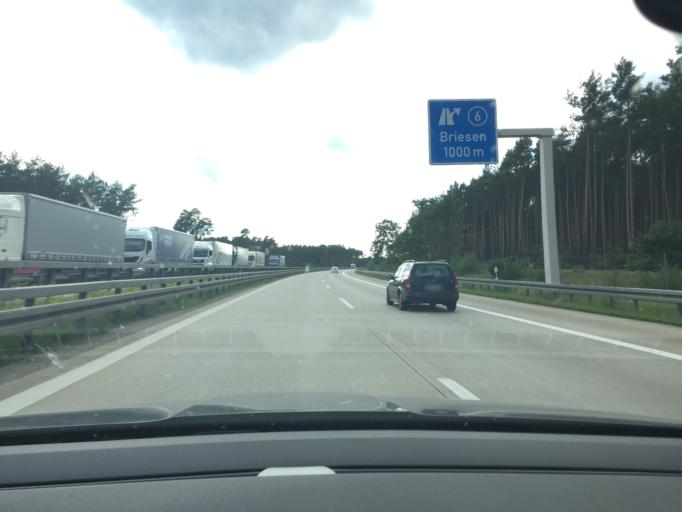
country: DE
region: Brandenburg
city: Briesen
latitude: 52.3243
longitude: 14.2926
